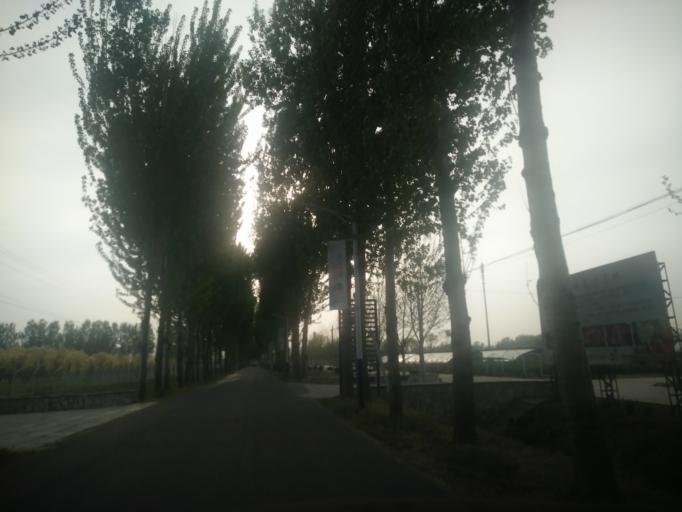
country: CN
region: Beijing
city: Weishanzhuang
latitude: 39.6756
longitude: 116.4413
